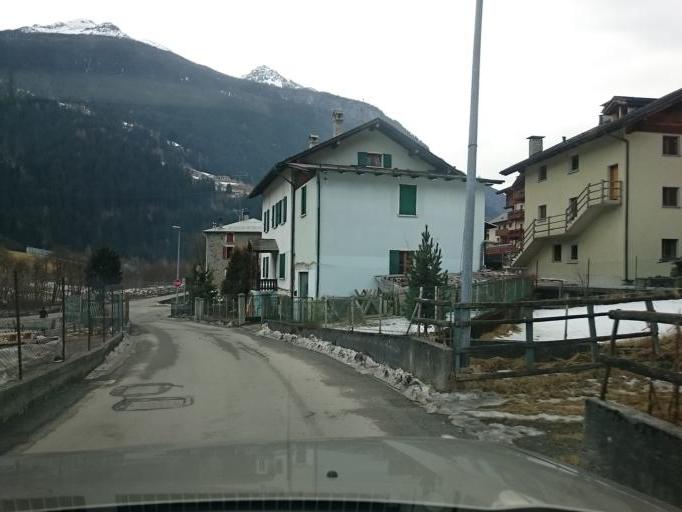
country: IT
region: Lombardy
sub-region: Provincia di Sondrio
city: Cepina
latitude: 46.4394
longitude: 10.3558
